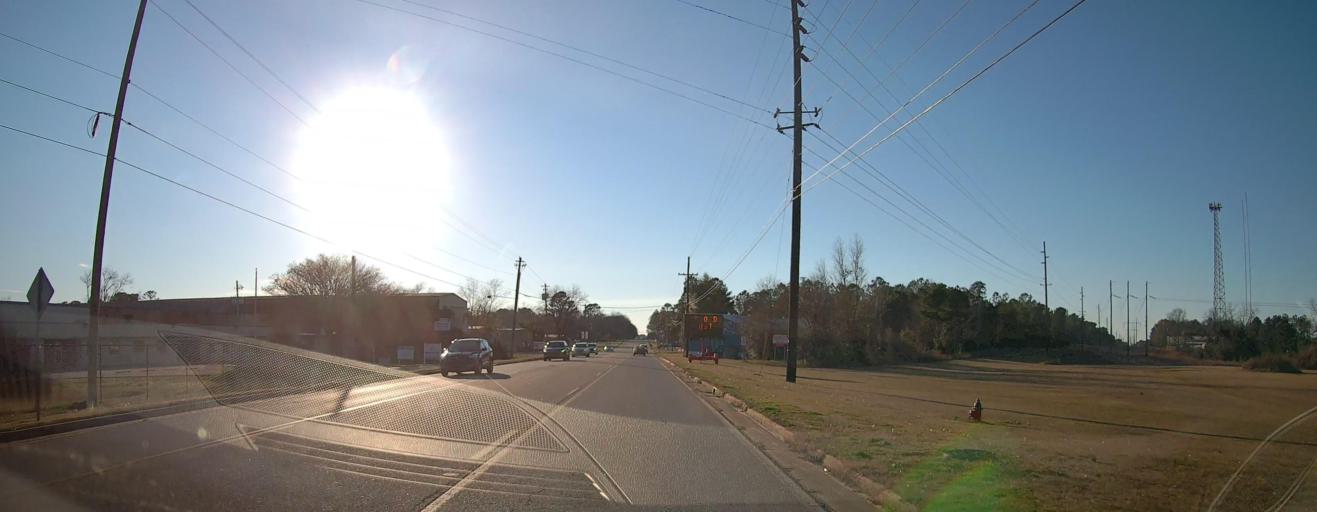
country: US
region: Georgia
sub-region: Dougherty County
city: Albany
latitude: 31.6227
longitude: -84.1900
